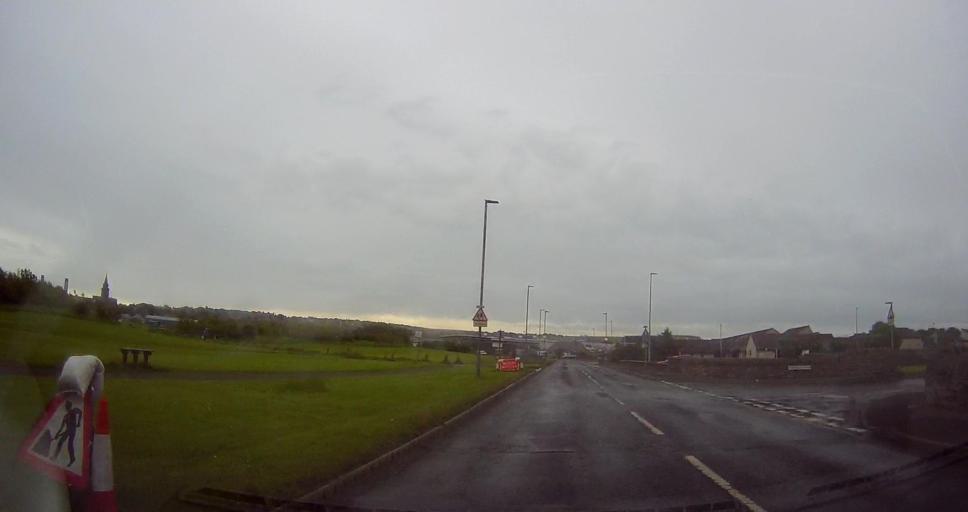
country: GB
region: Scotland
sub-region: Orkney Islands
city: Orkney
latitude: 58.9832
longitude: -2.9709
